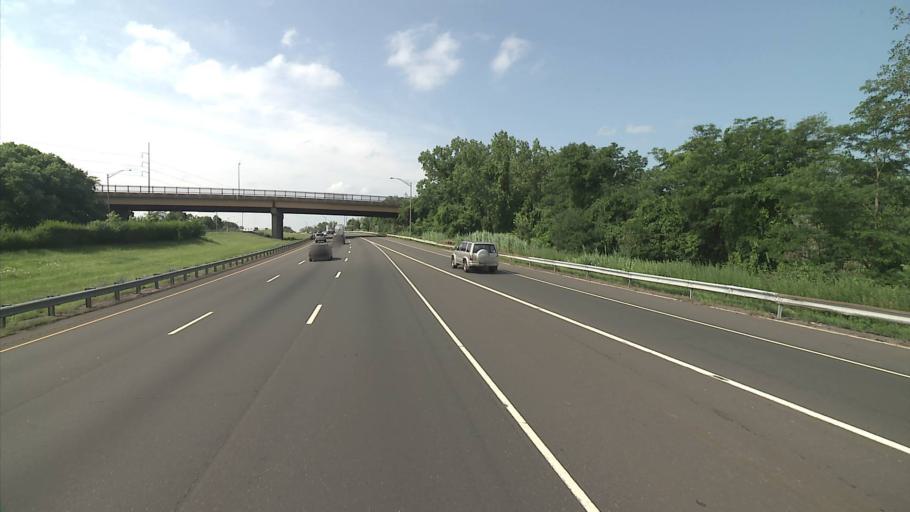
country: US
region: Connecticut
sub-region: New Haven County
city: North Haven
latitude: 41.3934
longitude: -72.8641
